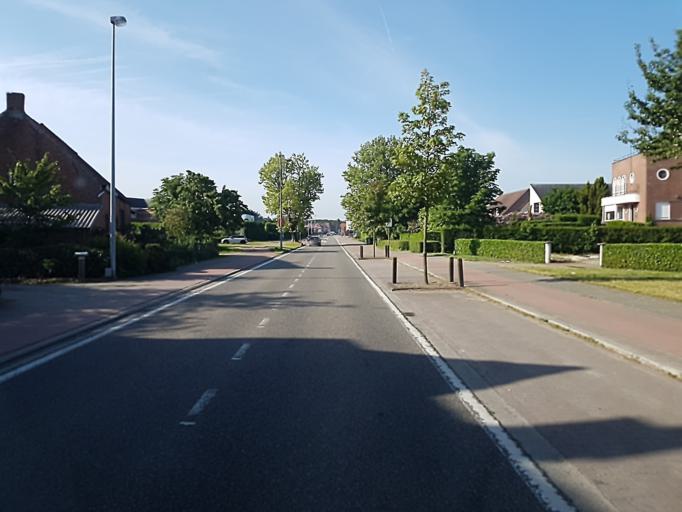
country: BE
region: Flanders
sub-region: Provincie Oost-Vlaanderen
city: Beveren
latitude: 51.2156
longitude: 4.1961
